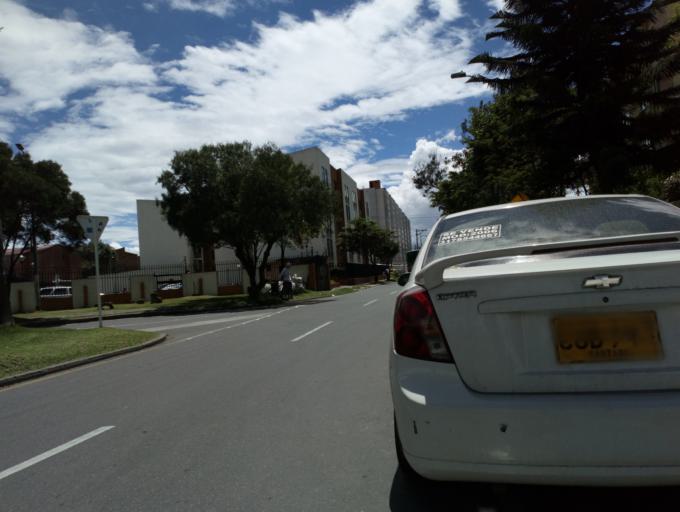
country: CO
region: Bogota D.C.
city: Bogota
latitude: 4.6137
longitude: -74.1511
